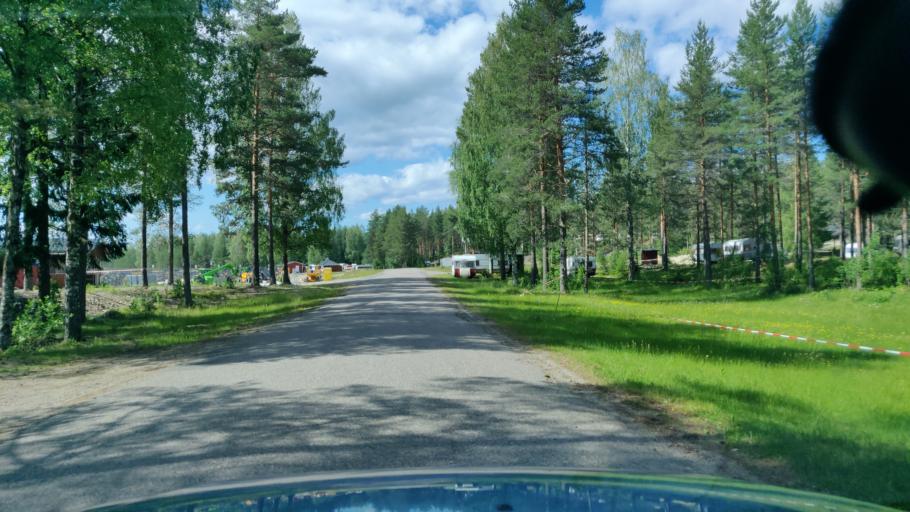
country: NO
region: Hedmark
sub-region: Trysil
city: Innbygda
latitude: 60.9173
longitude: 12.5581
